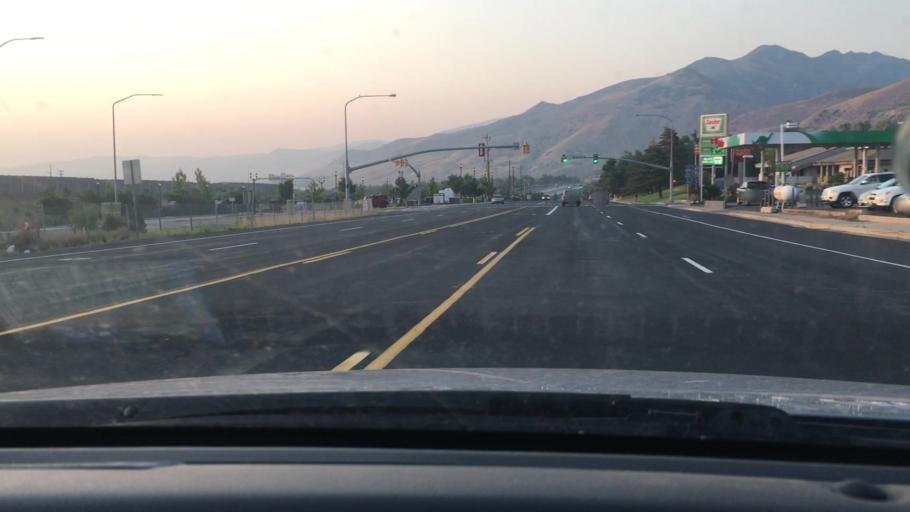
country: US
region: Utah
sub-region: Salt Lake County
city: Mount Olympus
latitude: 40.6861
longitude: -111.7960
